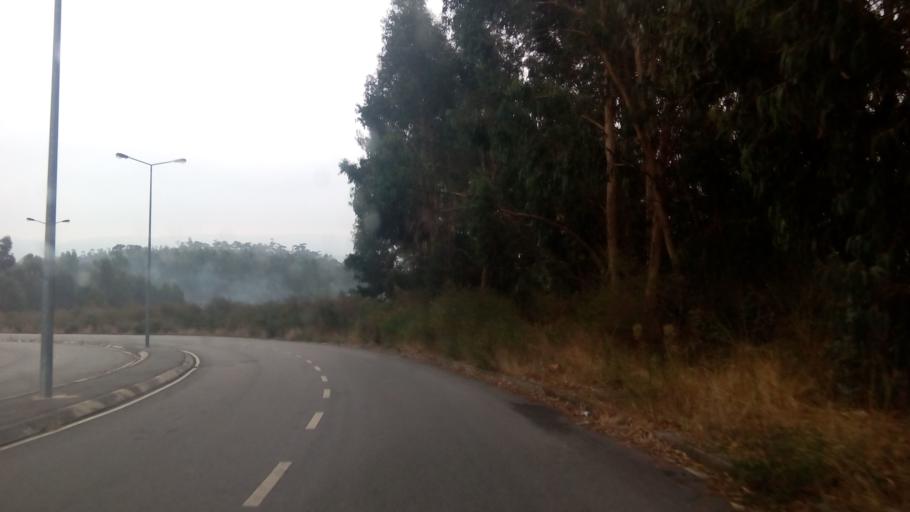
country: PT
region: Porto
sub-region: Paredes
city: Madalena
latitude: 41.2202
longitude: -8.3677
